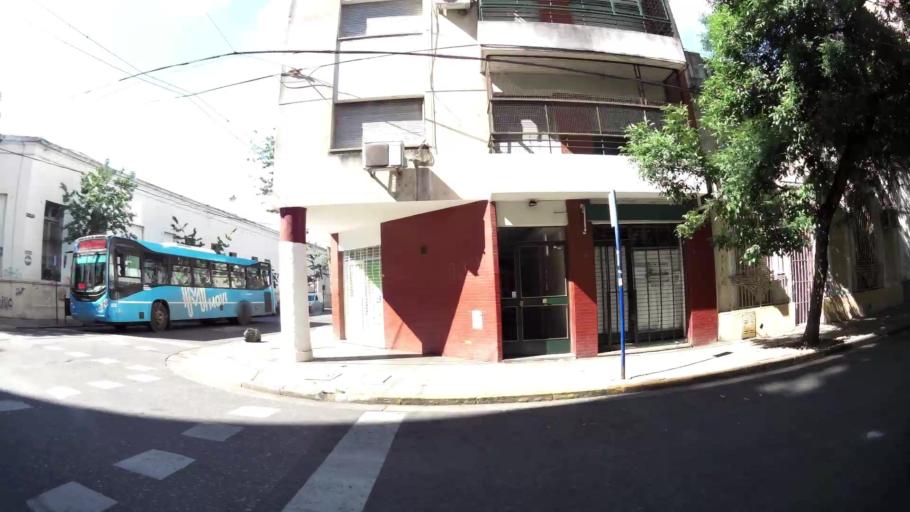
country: AR
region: Santa Fe
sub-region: Departamento de Rosario
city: Rosario
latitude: -32.9556
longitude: -60.6316
